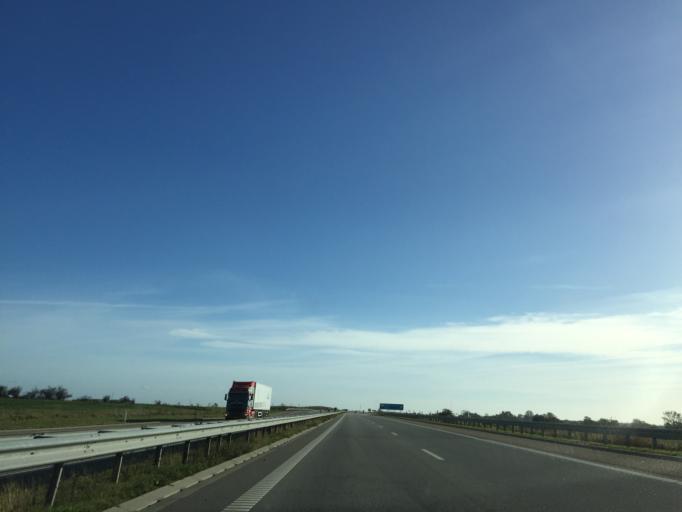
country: DK
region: South Denmark
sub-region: Sonderborg Kommune
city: Broager
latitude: 54.9359
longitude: 9.6845
